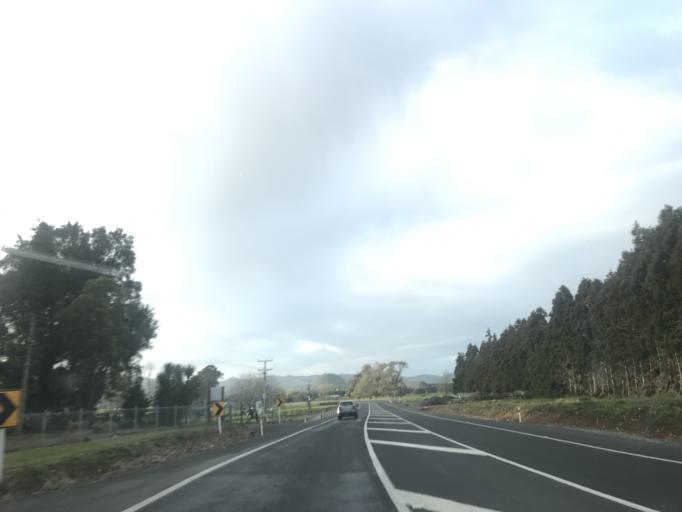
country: NZ
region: Waikato
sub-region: Hauraki District
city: Waihi
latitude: -37.4268
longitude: 175.8703
